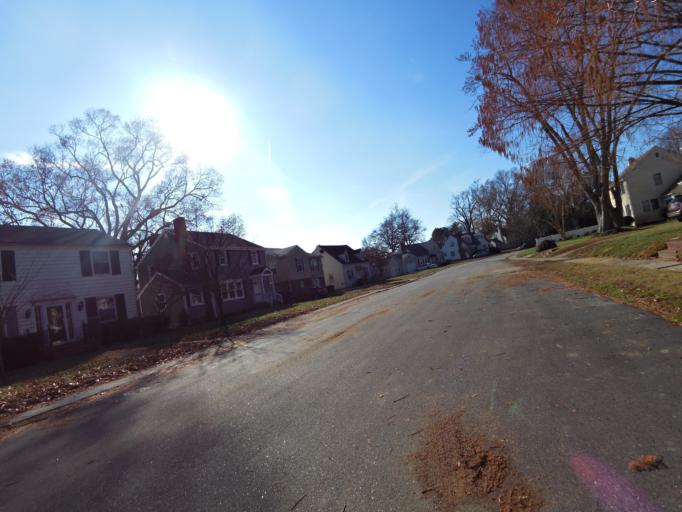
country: US
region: Virginia
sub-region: City of Hampton
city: Hampton
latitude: 36.9986
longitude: -76.3796
